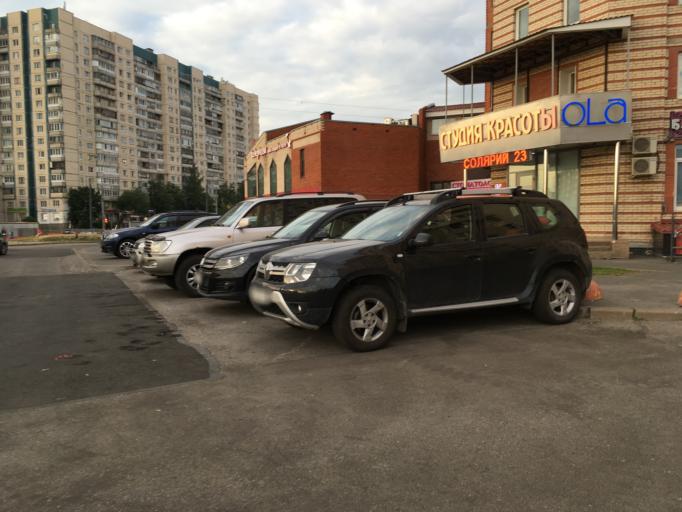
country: RU
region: St.-Petersburg
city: Staraya Derevnya
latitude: 60.0074
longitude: 30.2490
